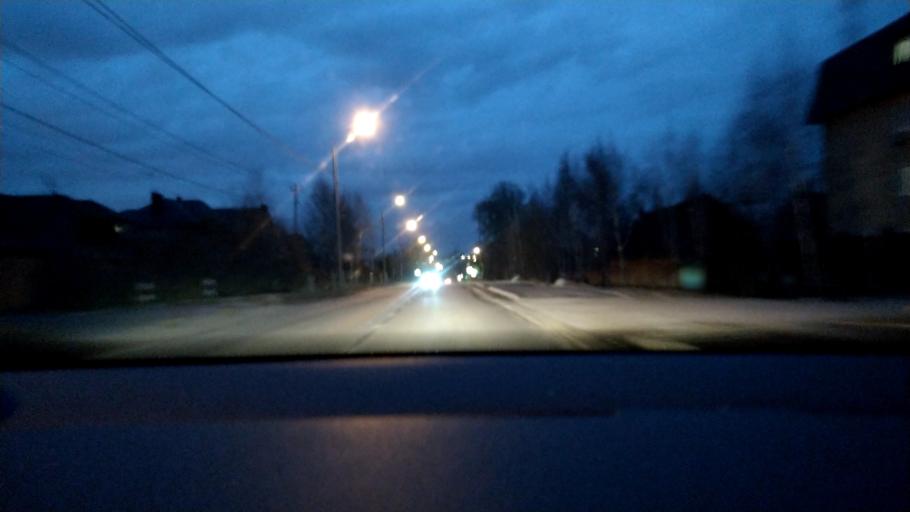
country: RU
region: Moscow
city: Vnukovo
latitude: 55.6002
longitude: 37.1997
